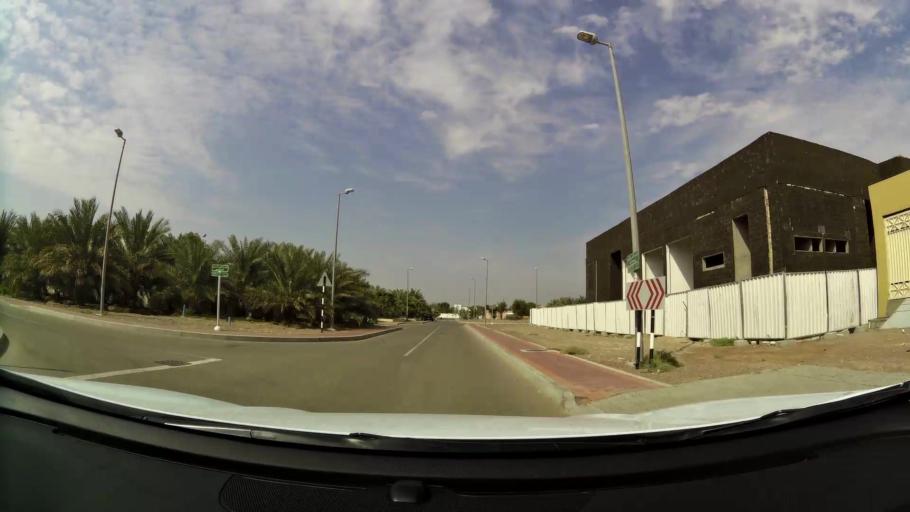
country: AE
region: Abu Dhabi
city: Al Ain
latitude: 24.0983
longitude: 55.8908
